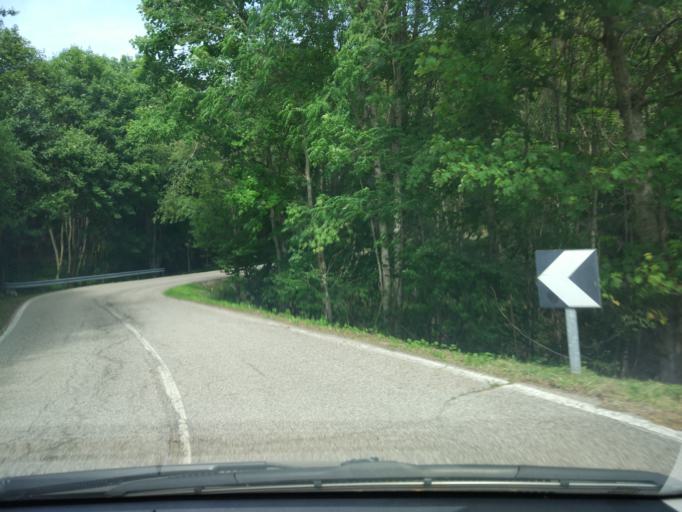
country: IT
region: Veneto
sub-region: Provincia di Verona
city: Ferrara di Monte Baldo
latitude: 45.6899
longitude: 10.8570
